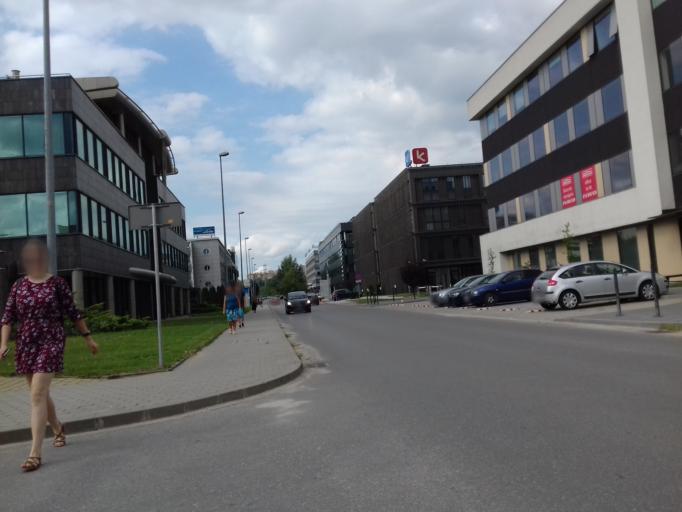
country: PL
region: Lesser Poland Voivodeship
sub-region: Krakow
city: Krakow
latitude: 50.0772
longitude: 19.9947
